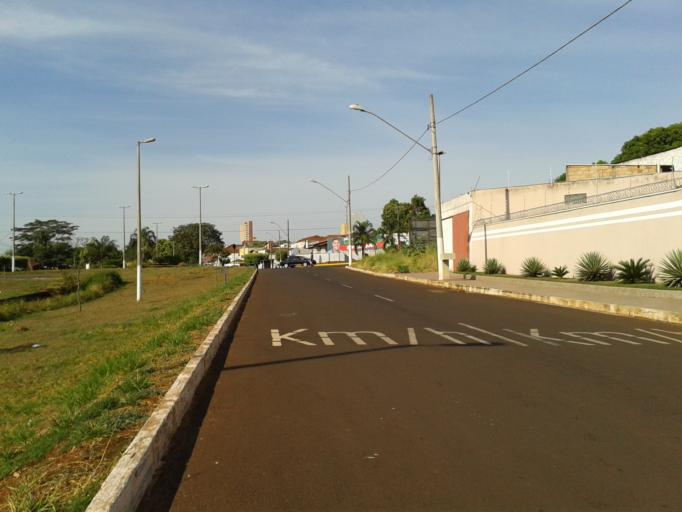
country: BR
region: Minas Gerais
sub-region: Ituiutaba
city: Ituiutaba
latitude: -18.9657
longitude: -49.4608
